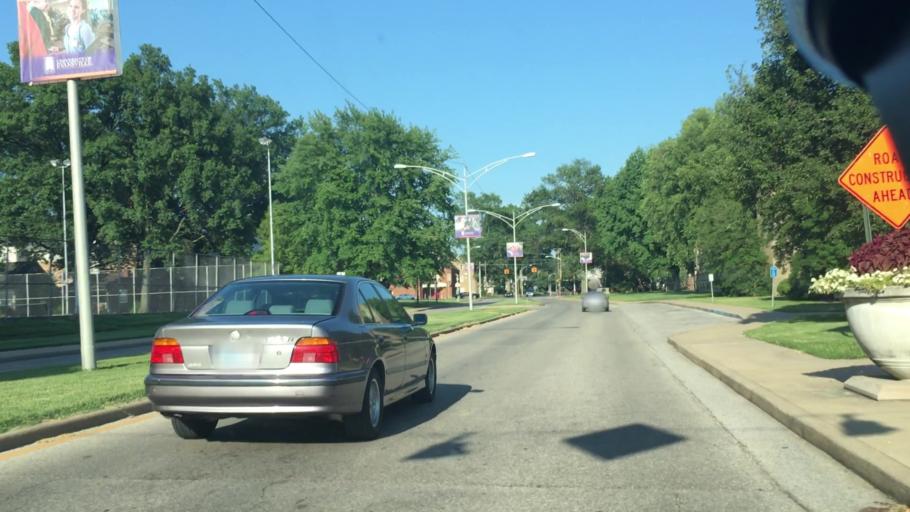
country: US
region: Indiana
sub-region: Vanderburgh County
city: Evansville
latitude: 37.9734
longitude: -87.5312
